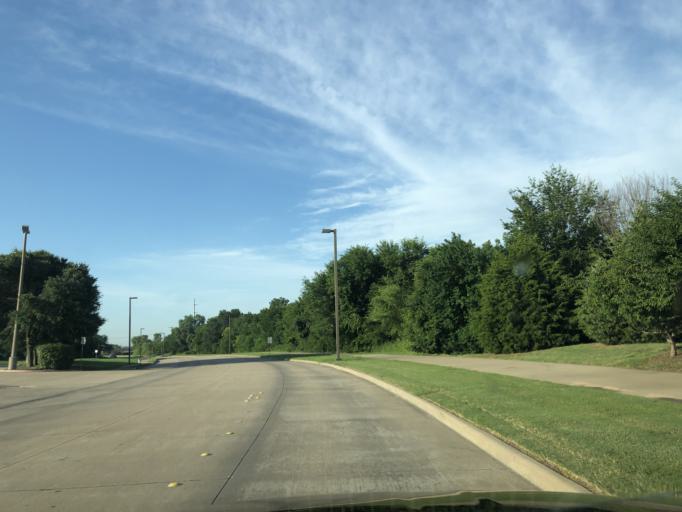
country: US
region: Texas
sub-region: Dallas County
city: Sunnyvale
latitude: 32.8442
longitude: -96.6022
